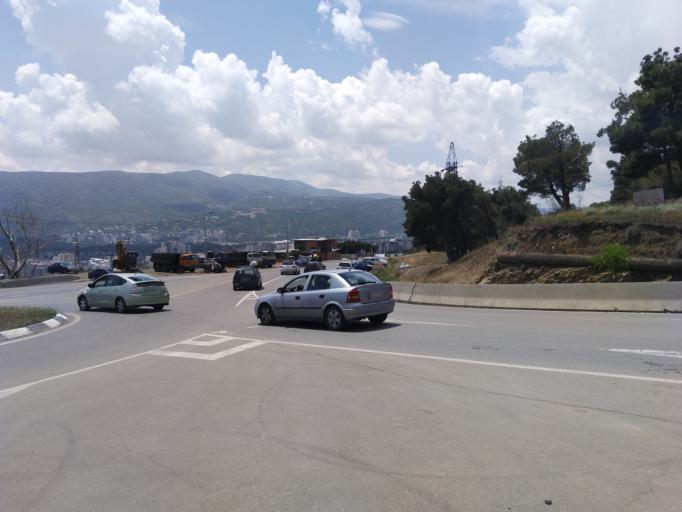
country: GE
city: Tsqnet'i
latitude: 41.7360
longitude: 44.7471
